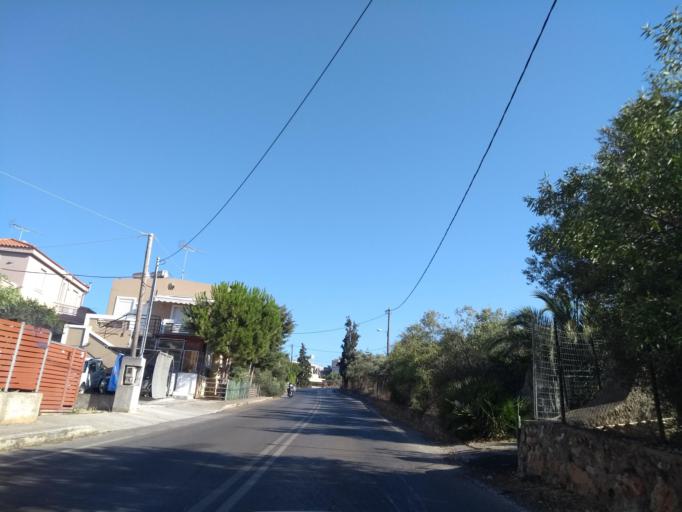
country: GR
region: Crete
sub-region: Nomos Chanias
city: Pithari
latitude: 35.5368
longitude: 24.0814
